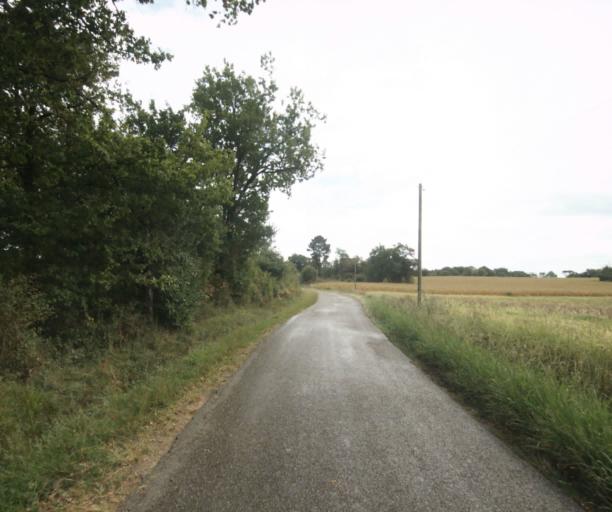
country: FR
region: Midi-Pyrenees
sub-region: Departement du Gers
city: Cazaubon
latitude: 43.8957
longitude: -0.1229
